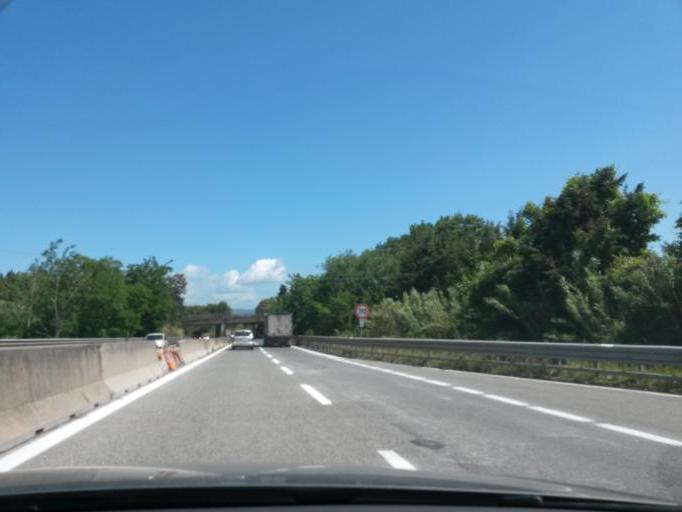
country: IT
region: Tuscany
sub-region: Provincia di Livorno
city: La California
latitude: 43.2977
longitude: 10.5465
